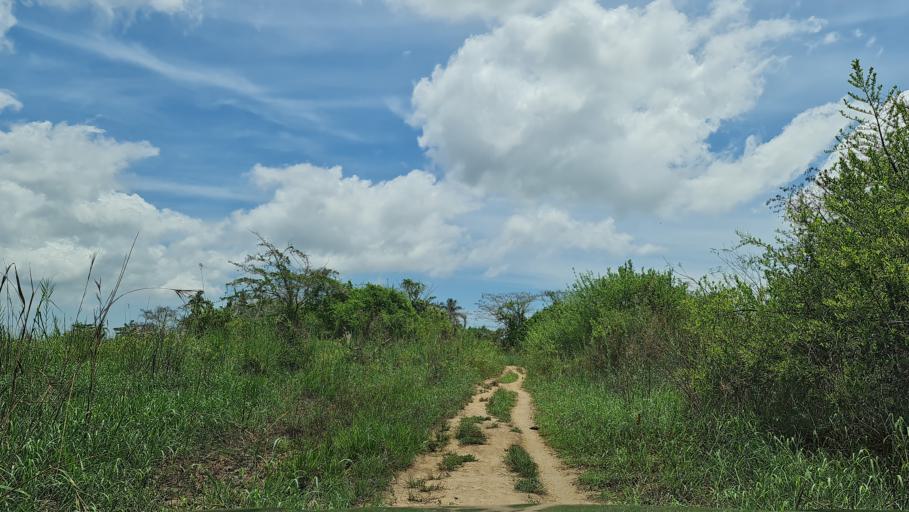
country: MZ
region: Zambezia
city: Quelimane
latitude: -17.5836
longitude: 37.3800
